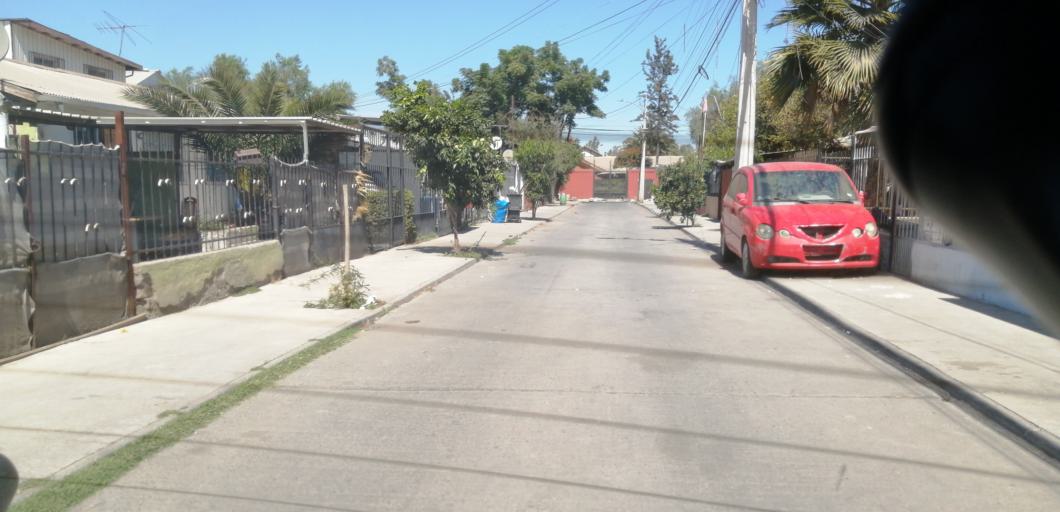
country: CL
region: Santiago Metropolitan
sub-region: Provincia de Santiago
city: Lo Prado
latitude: -33.4349
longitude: -70.7524
